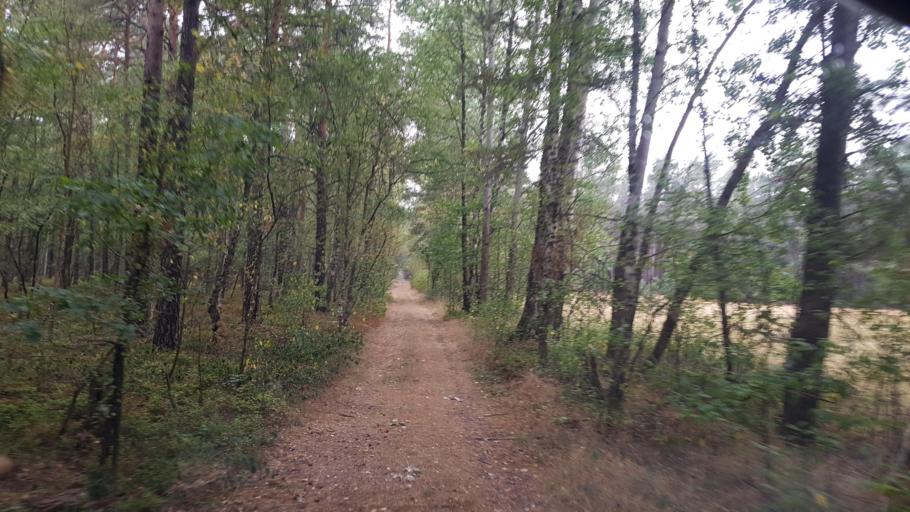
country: DE
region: Brandenburg
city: Sallgast
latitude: 51.6041
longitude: 13.8267
